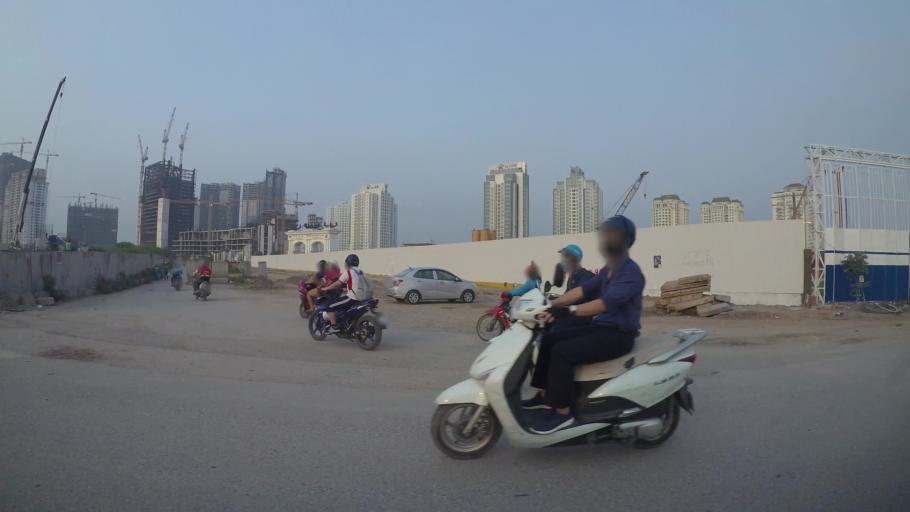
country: VN
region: Ha Noi
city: Tay Ho
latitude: 21.0789
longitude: 105.7881
